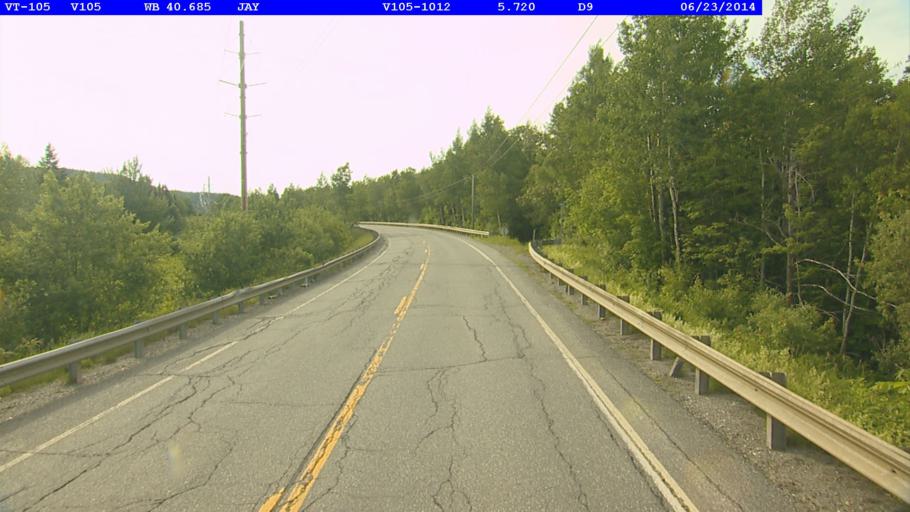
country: CA
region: Quebec
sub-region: Monteregie
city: Sutton
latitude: 44.9759
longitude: -72.4719
